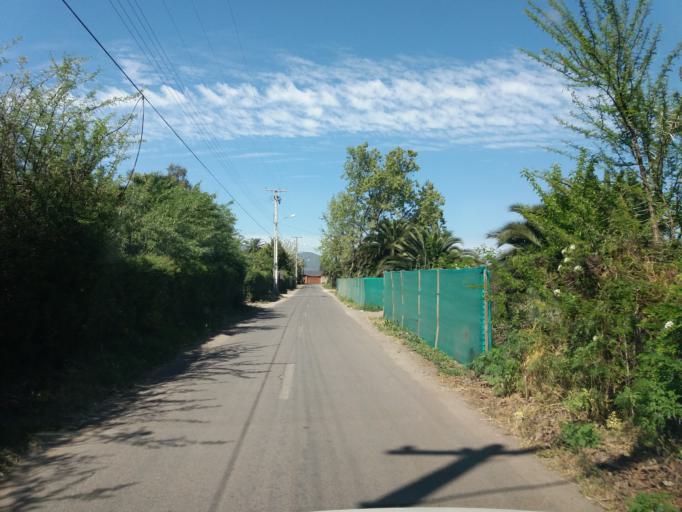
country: CL
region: Valparaiso
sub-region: Provincia de Quillota
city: Quillota
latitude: -32.8718
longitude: -71.2155
